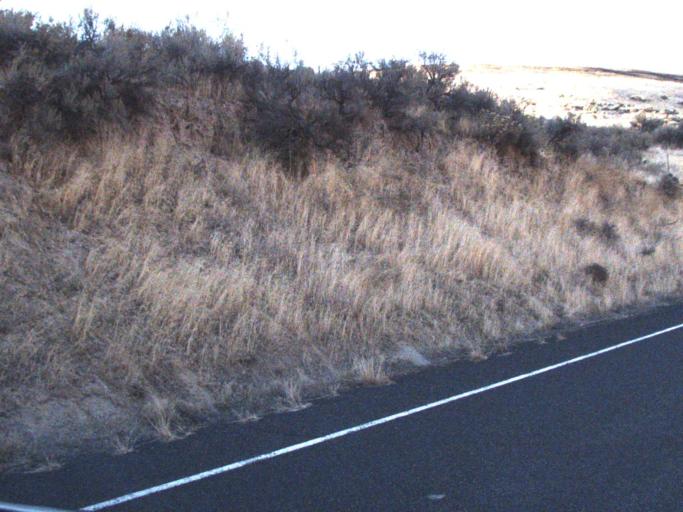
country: US
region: Washington
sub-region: Franklin County
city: Connell
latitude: 46.6695
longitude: -118.5467
